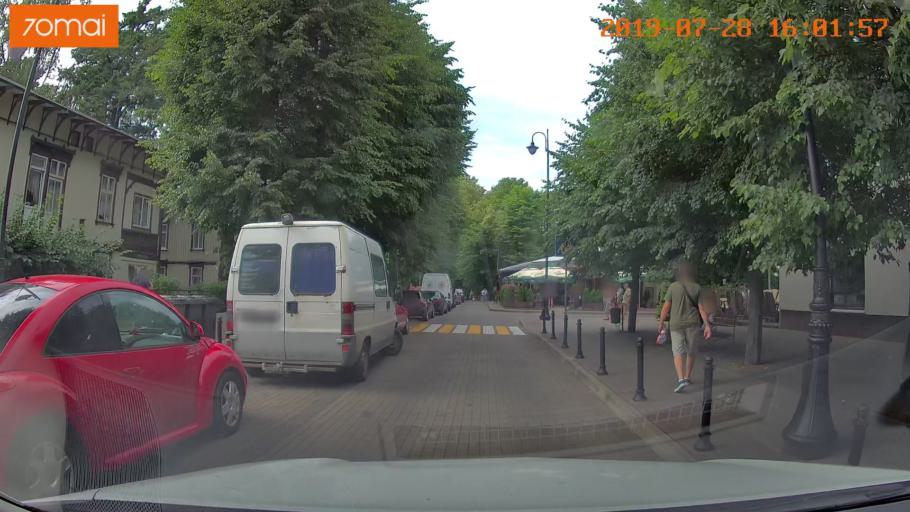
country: RU
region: Kaliningrad
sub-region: Gorod Svetlogorsk
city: Svetlogorsk
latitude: 54.9444
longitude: 20.1528
